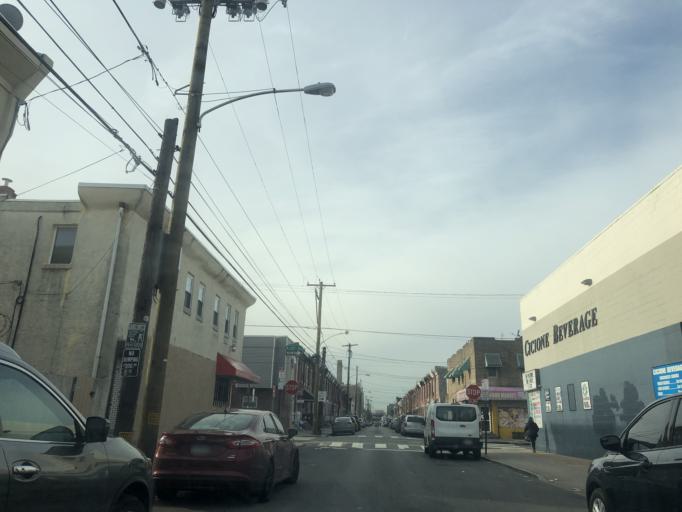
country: US
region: Pennsylvania
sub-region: Philadelphia County
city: Philadelphia
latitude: 39.9292
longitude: -75.1780
